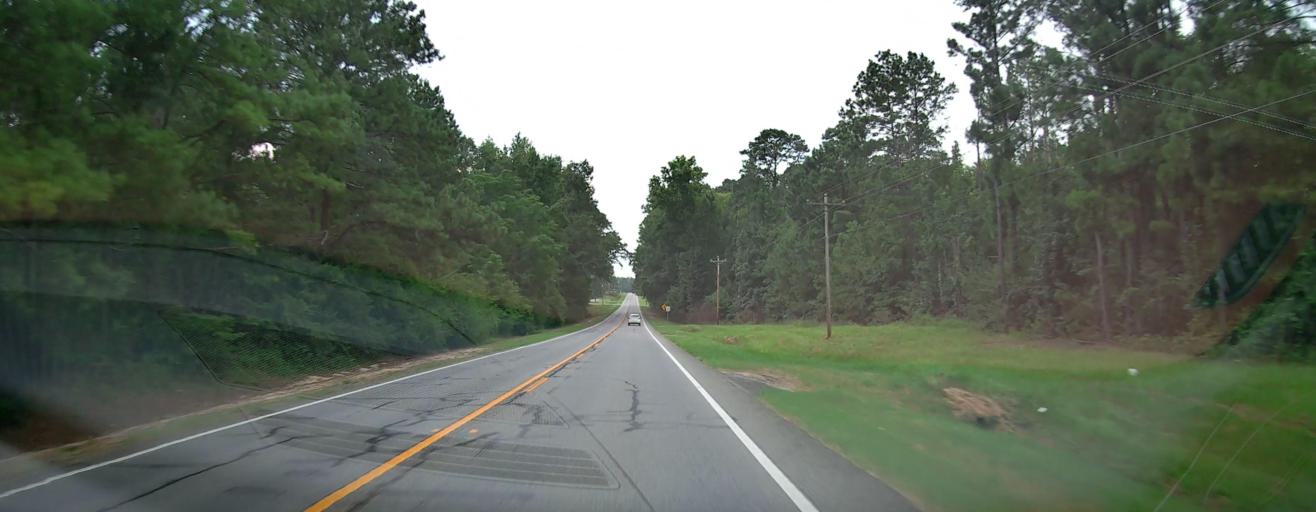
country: US
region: Georgia
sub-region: Laurens County
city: East Dublin
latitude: 32.5853
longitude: -82.8339
